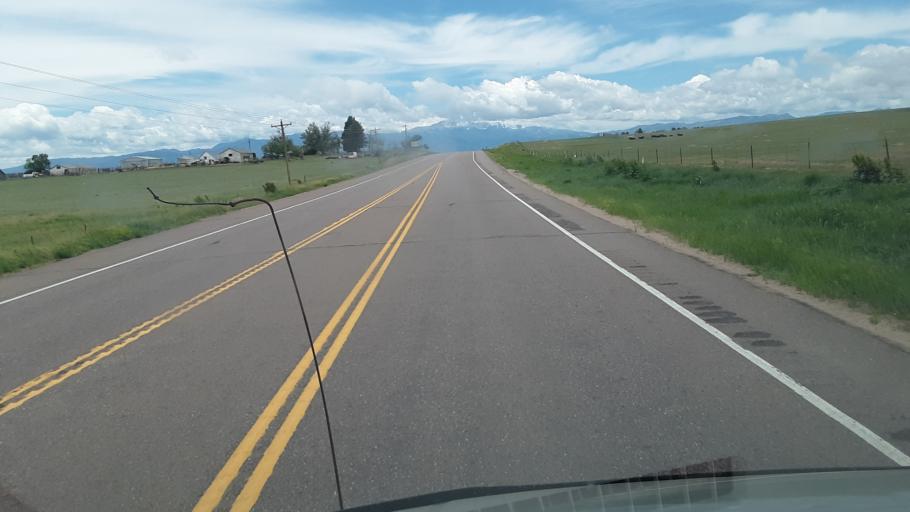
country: US
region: Colorado
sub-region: El Paso County
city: Cimarron Hills
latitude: 38.8387
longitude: -104.5583
